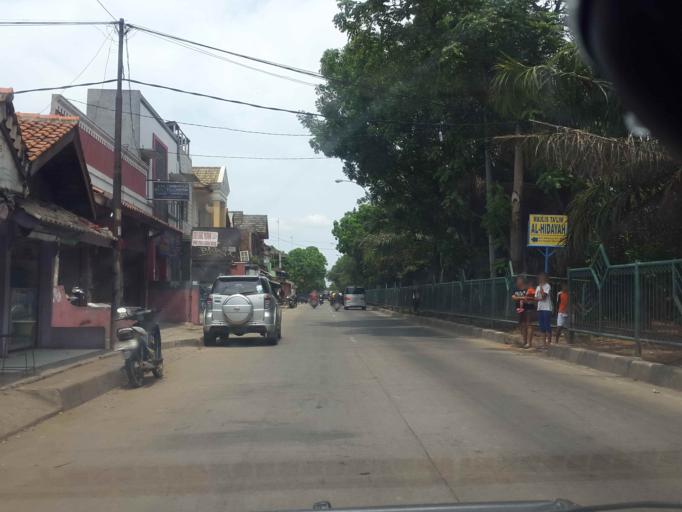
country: ID
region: Banten
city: Tangerang
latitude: -6.1561
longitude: 106.6323
